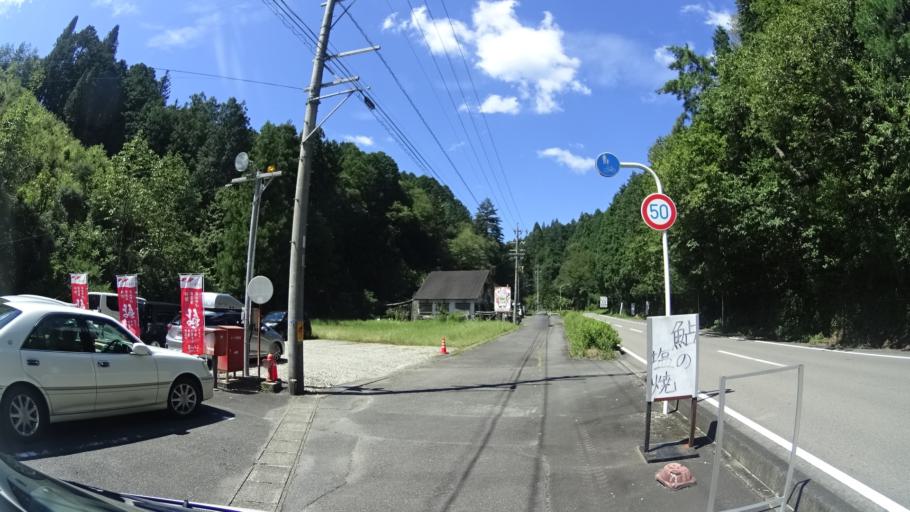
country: JP
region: Gifu
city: Minokamo
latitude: 35.5927
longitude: 137.0849
